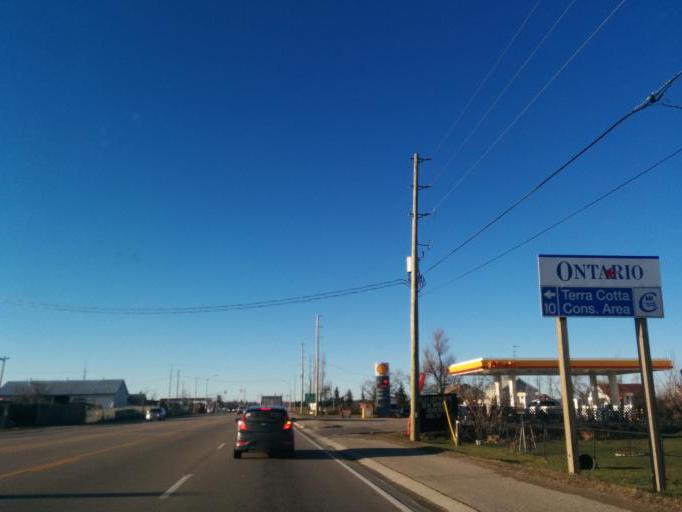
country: CA
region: Ontario
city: Brampton
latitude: 43.7720
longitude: -79.8762
